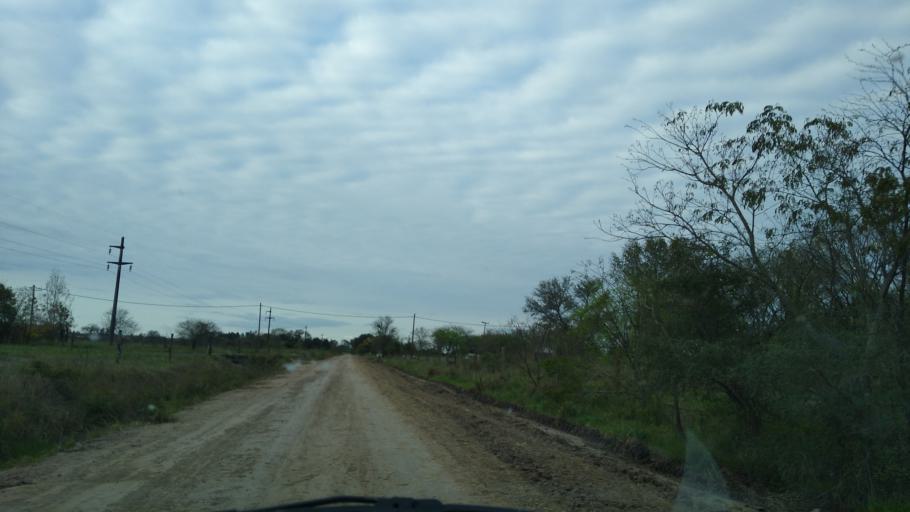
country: AR
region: Chaco
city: Fontana
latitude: -27.3859
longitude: -59.0446
